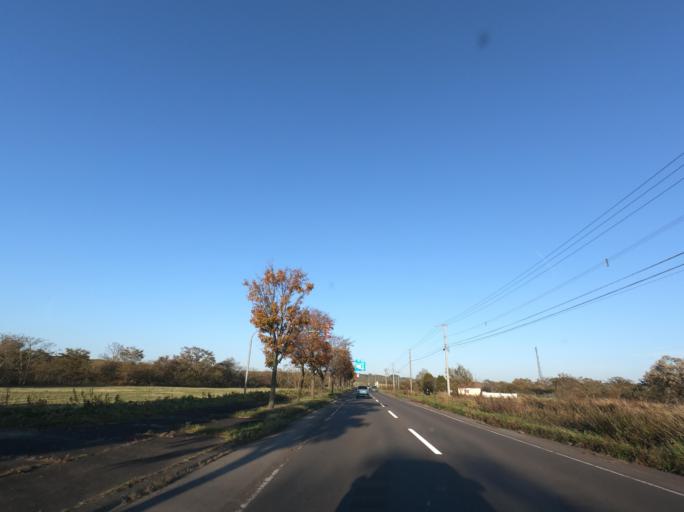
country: JP
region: Hokkaido
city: Kushiro
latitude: 43.0737
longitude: 144.2350
